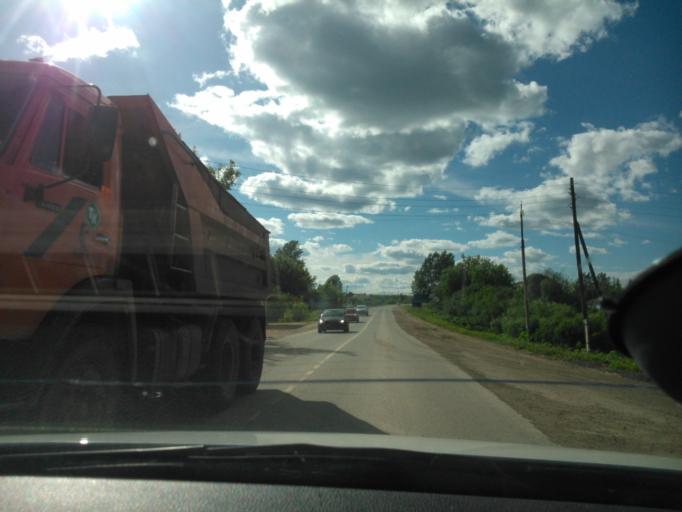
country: RU
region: Perm
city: Ust'-Kachka
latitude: 57.9420
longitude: 55.7472
